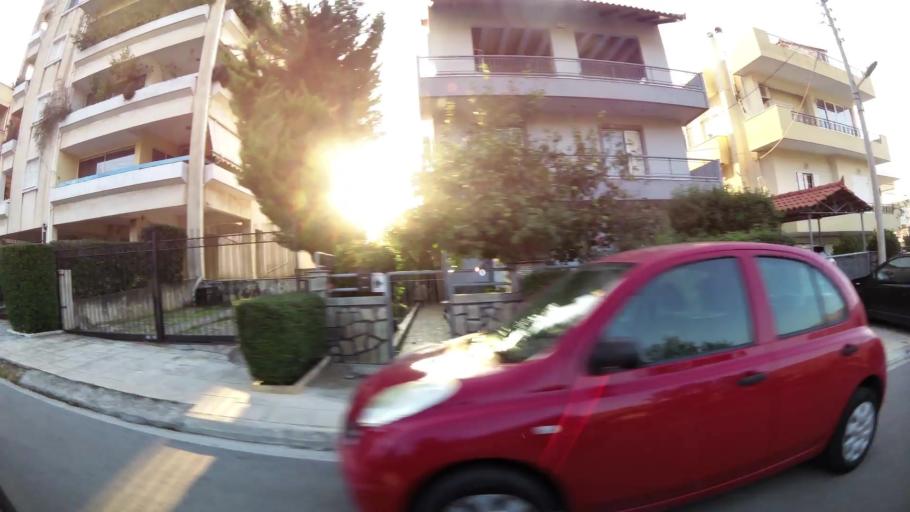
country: GR
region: Attica
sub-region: Nomarchia Athinas
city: Argyroupoli
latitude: 37.8953
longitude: 23.7754
